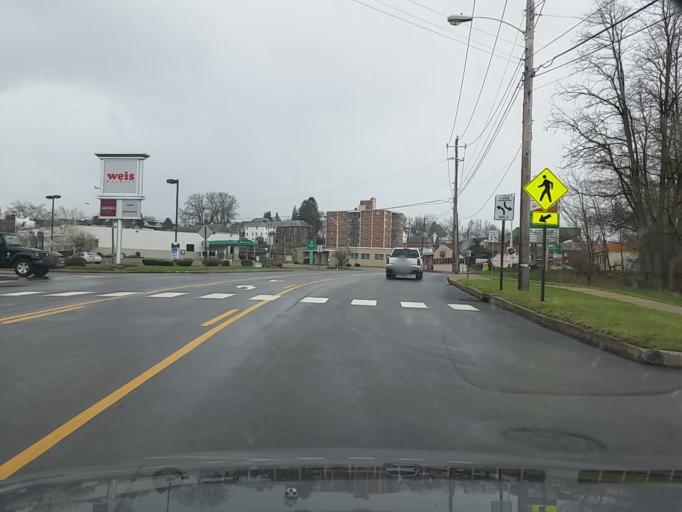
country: US
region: Pennsylvania
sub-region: Luzerne County
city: Nanticoke
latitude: 41.2077
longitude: -76.0041
